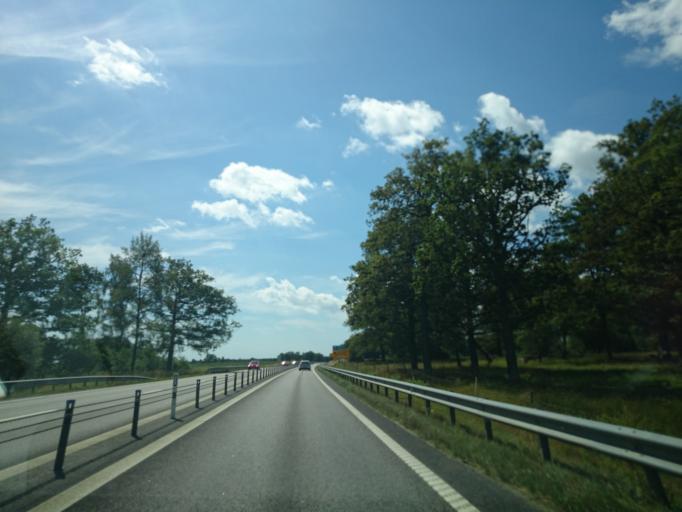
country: SE
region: Kalmar
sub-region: Kalmar Kommun
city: Lindsdal
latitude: 56.8138
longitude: 16.3691
